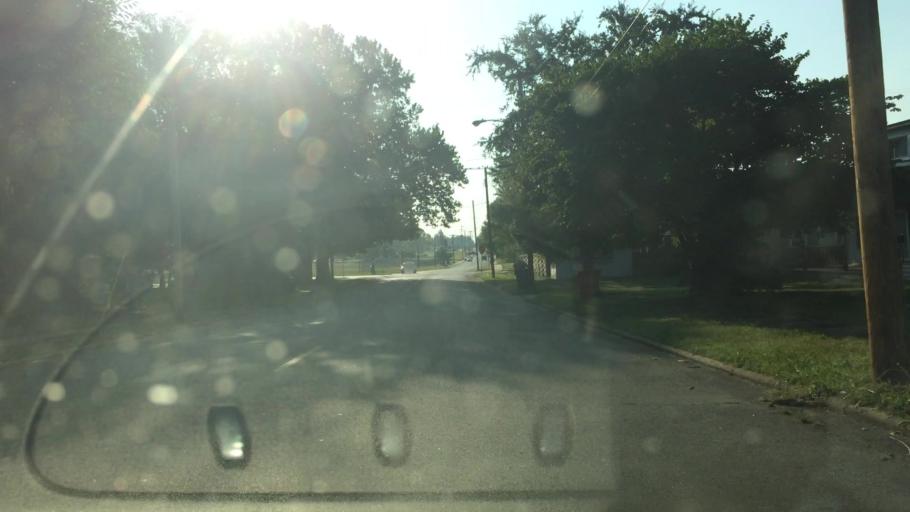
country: US
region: Missouri
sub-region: Greene County
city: Springfield
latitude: 37.2186
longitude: -93.2719
